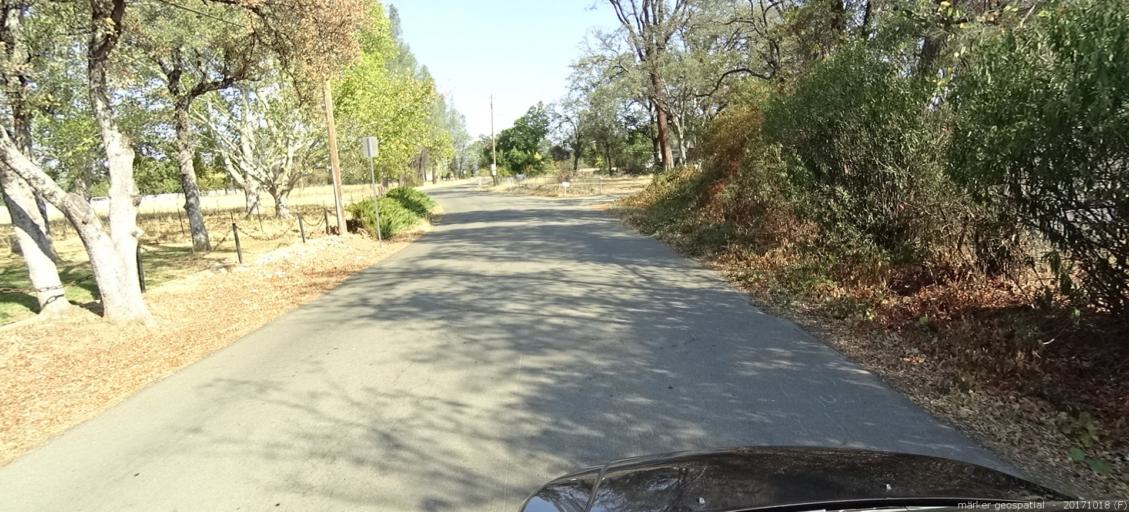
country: US
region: California
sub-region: Shasta County
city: Palo Cedro
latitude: 40.5724
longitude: -122.2371
